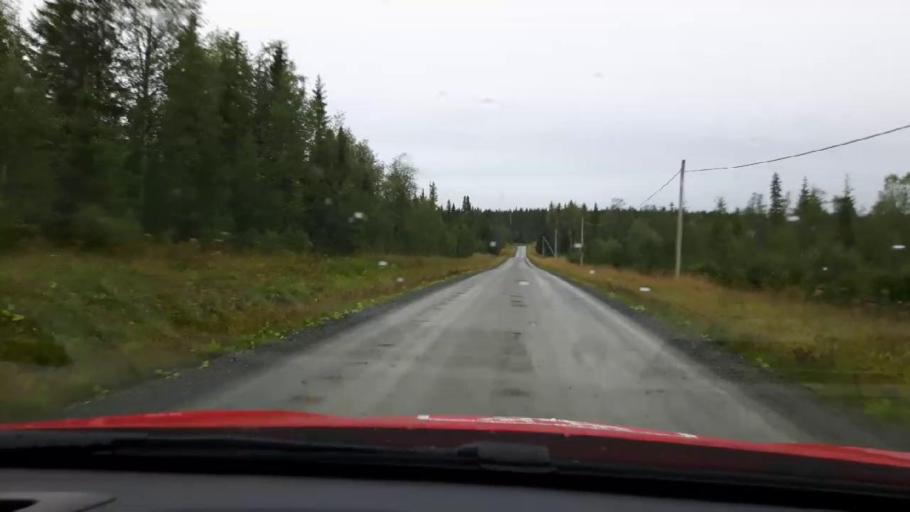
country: SE
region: Jaemtland
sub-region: Are Kommun
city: Are
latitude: 63.4390
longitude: 12.8075
